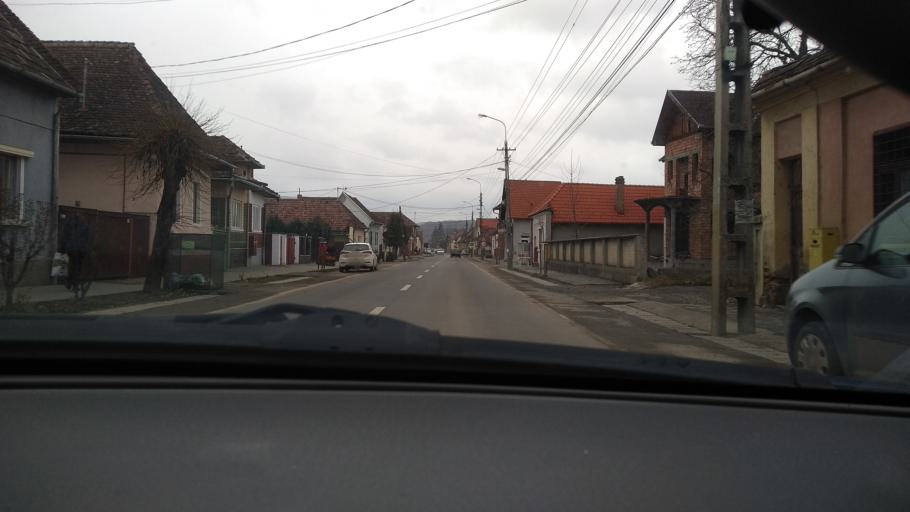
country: RO
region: Mures
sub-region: Comuna Miercurea Nirajului
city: Miercurea Nirajului
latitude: 46.5336
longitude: 24.7966
